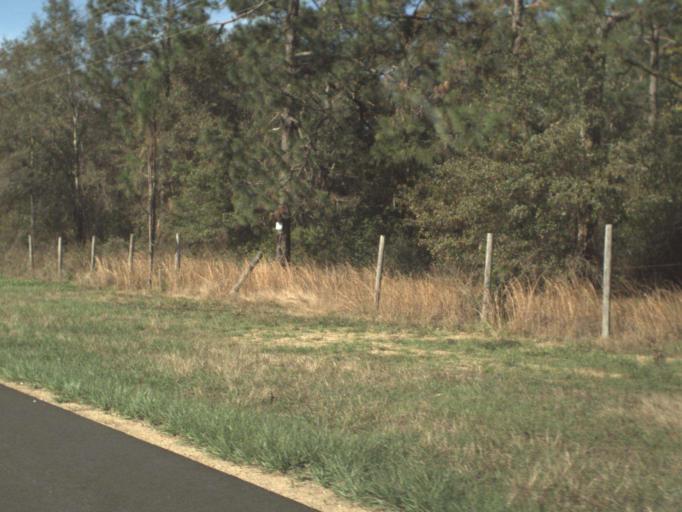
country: US
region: Alabama
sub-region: Escambia County
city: East Brewton
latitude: 30.8978
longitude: -86.9935
